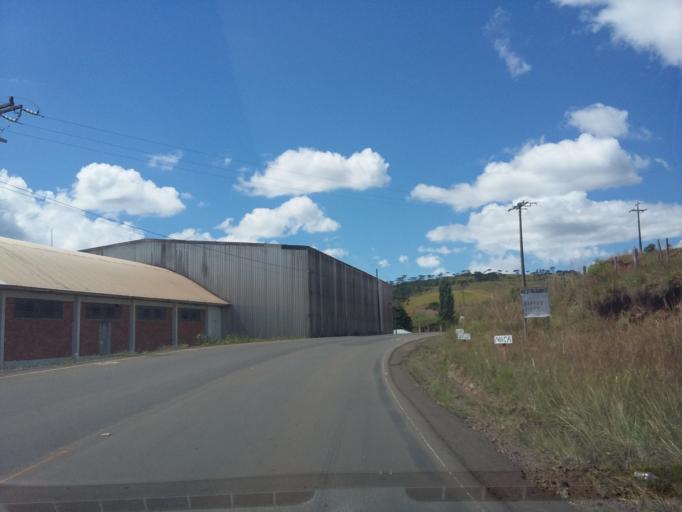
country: BR
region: Santa Catarina
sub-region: Lauro Muller
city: Lauro Muller
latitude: -28.3379
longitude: -49.6489
